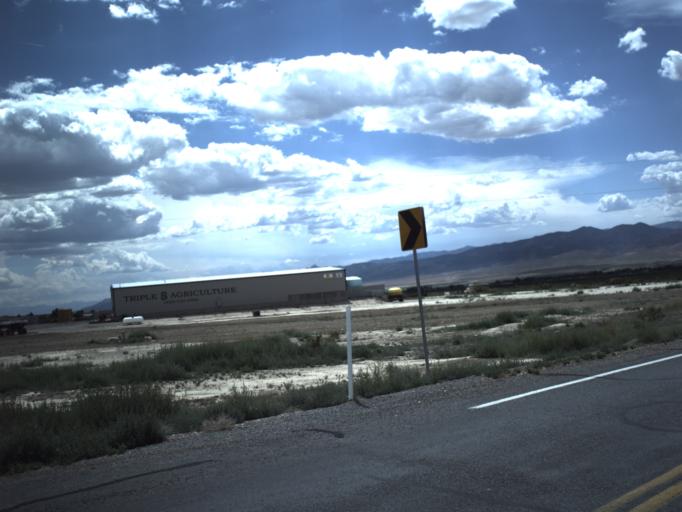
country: US
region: Utah
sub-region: Sanpete County
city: Centerfield
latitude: 39.1356
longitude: -111.7776
